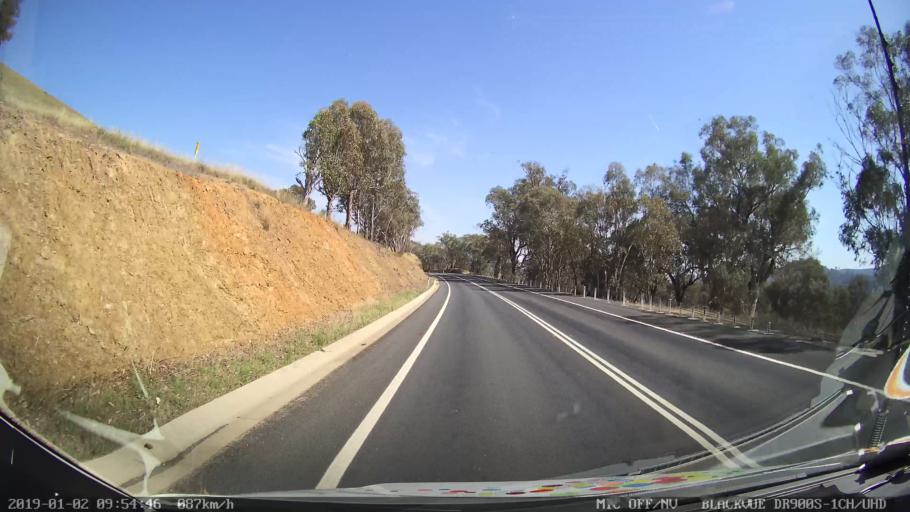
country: AU
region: New South Wales
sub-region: Tumut Shire
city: Tumut
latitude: -35.2308
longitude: 148.1950
